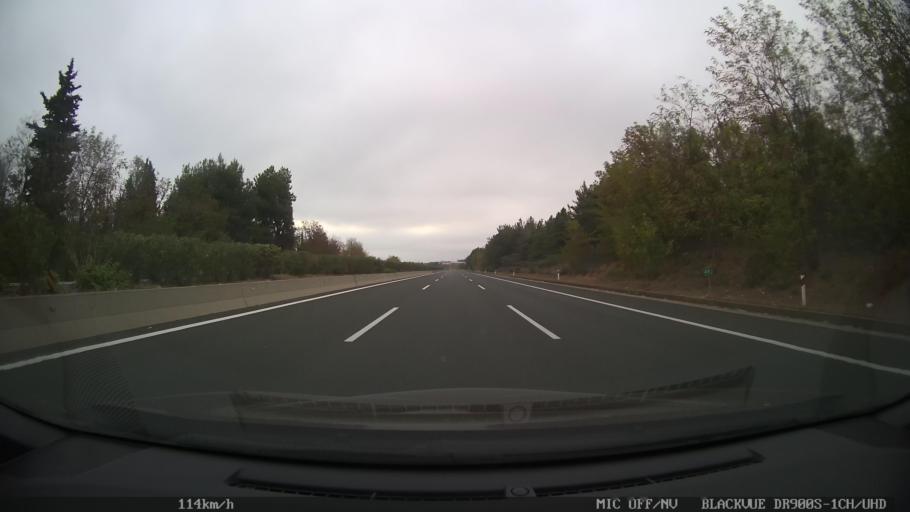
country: GR
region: Central Macedonia
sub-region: Nomos Pierias
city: Aiginio
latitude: 40.4776
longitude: 22.5698
